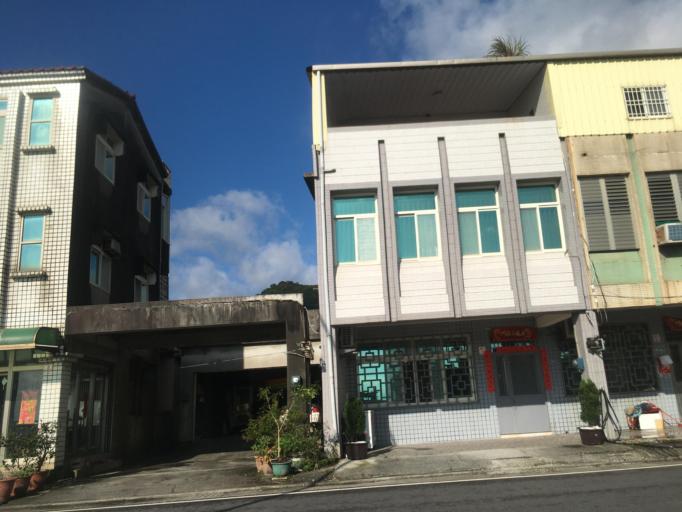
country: TW
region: Taiwan
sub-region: Yilan
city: Yilan
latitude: 24.9006
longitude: 121.8634
